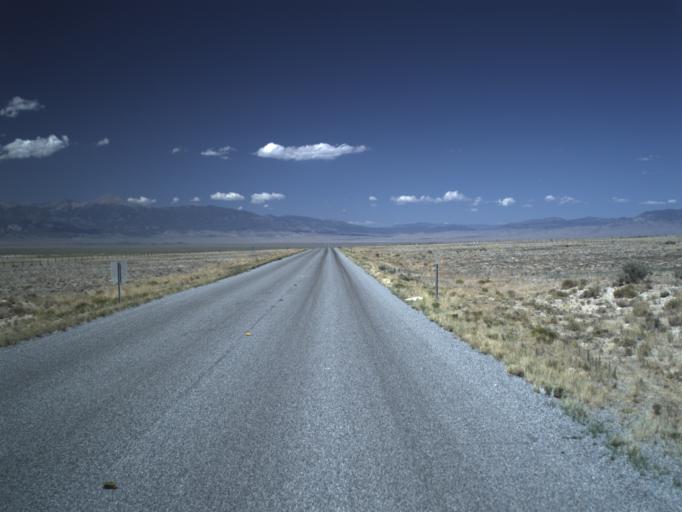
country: US
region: Nevada
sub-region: White Pine County
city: McGill
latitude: 39.0400
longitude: -113.8254
